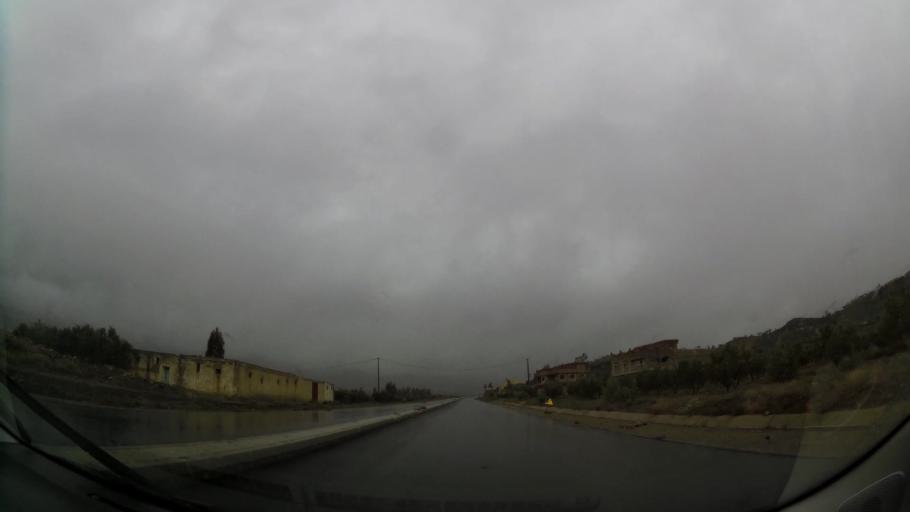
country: MA
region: Oriental
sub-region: Nador
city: Midar
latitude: 34.8325
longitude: -3.7198
